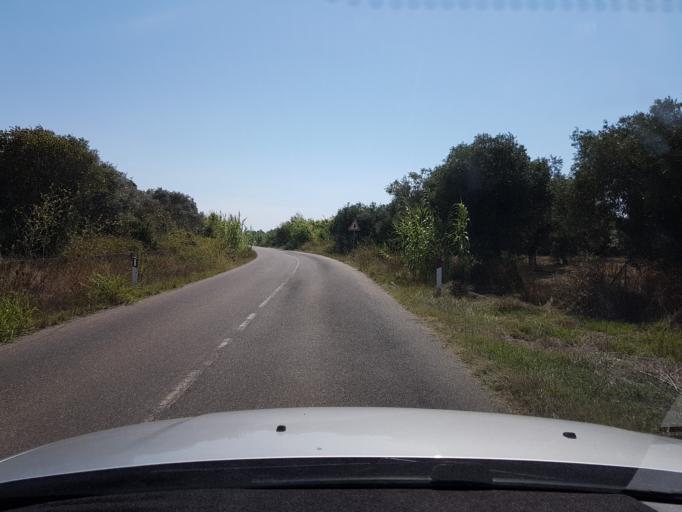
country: IT
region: Sardinia
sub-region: Provincia di Oristano
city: Nurachi
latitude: 39.9552
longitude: 8.5331
